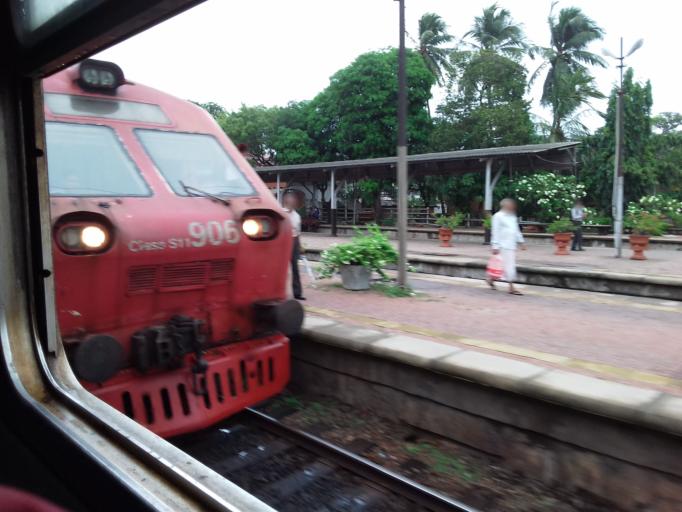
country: LK
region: Western
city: Colombo
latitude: 6.9332
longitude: 79.8520
